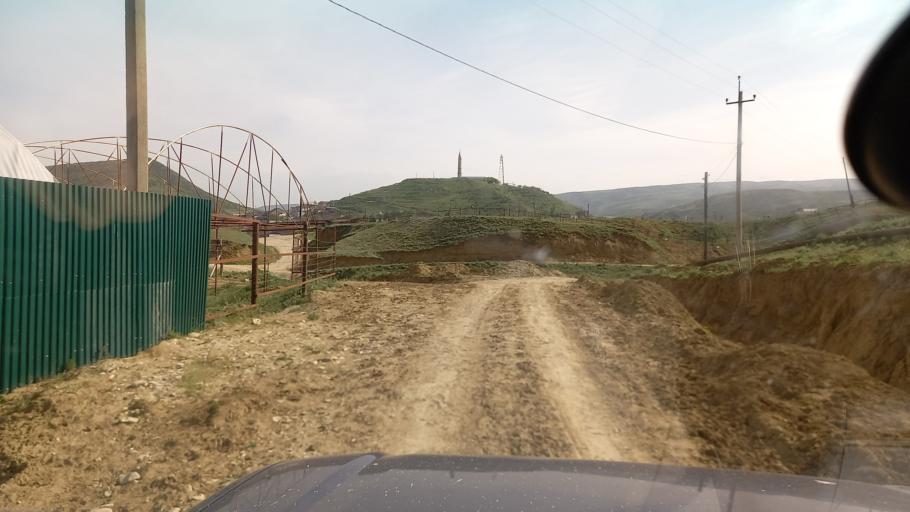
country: RU
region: Dagestan
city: Karabudakhkent
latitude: 42.7171
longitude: 47.5669
